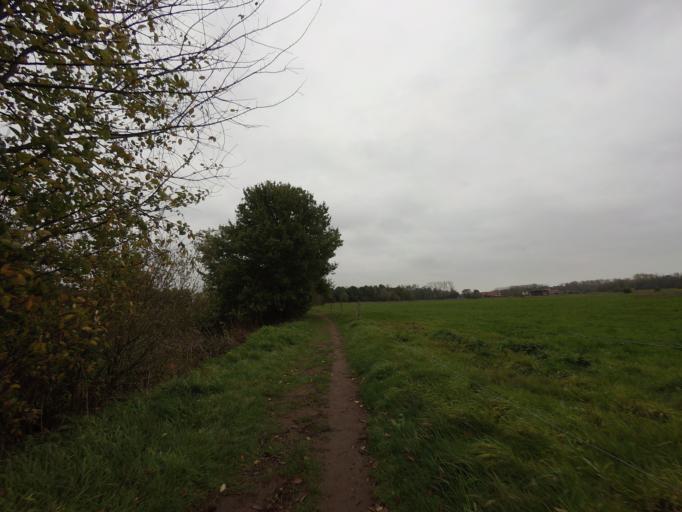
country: BE
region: Flanders
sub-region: Provincie Antwerpen
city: Bonheiden
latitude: 51.0231
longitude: 4.5213
